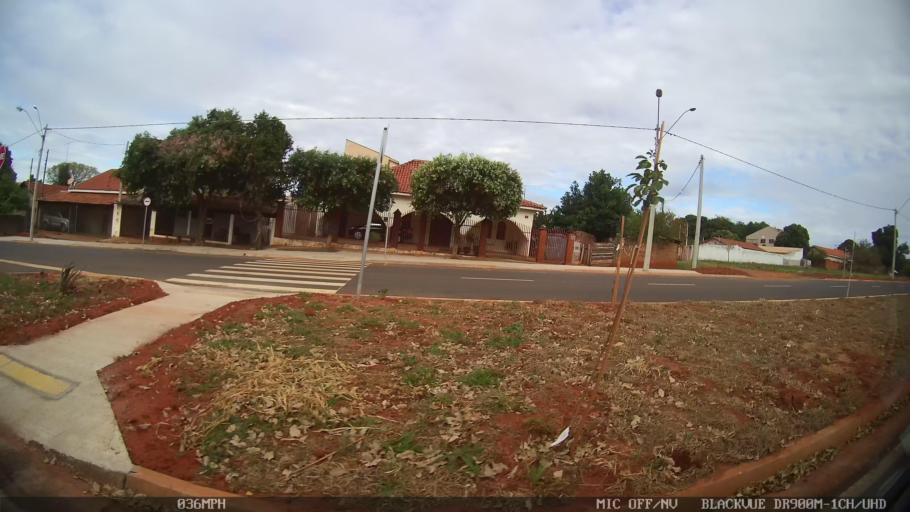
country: BR
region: Sao Paulo
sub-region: Sao Jose Do Rio Preto
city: Sao Jose do Rio Preto
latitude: -20.8284
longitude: -49.4124
